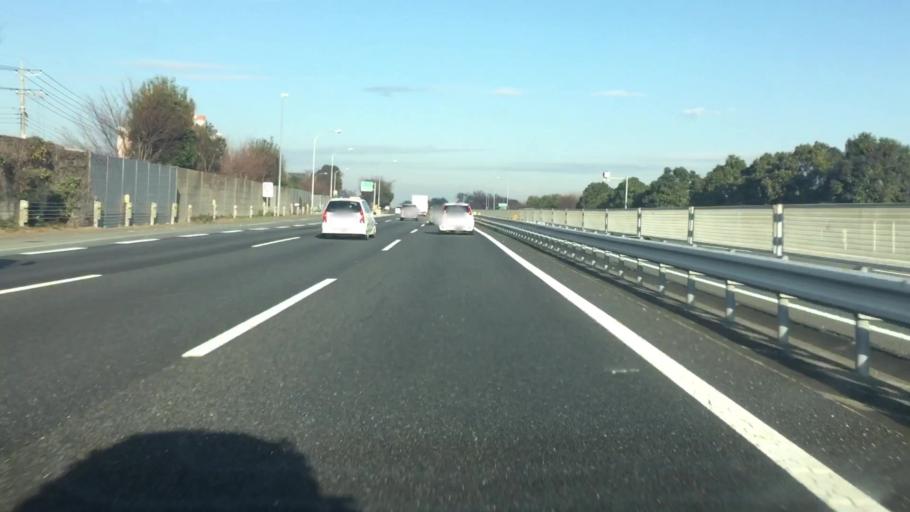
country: JP
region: Saitama
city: Honjo
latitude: 36.2154
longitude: 139.1667
